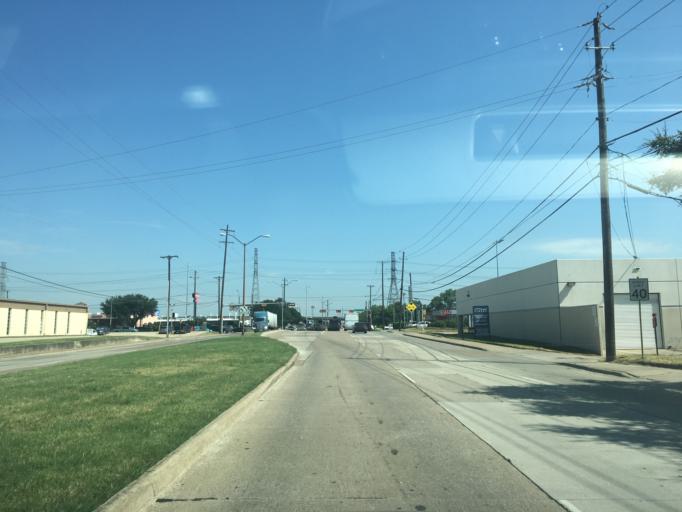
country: US
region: Texas
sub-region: Dallas County
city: Garland
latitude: 32.8628
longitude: -96.6657
